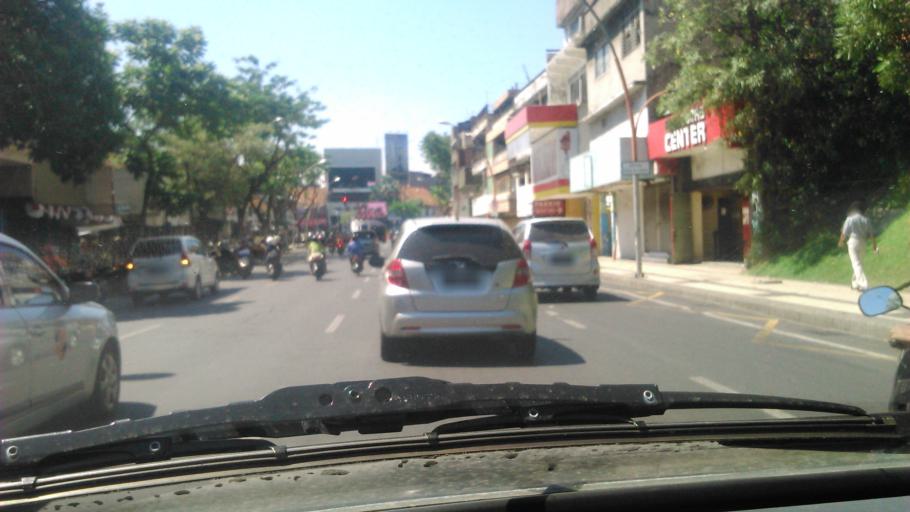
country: ID
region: East Java
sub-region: Kota Surabaya
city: Surabaya
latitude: -7.2575
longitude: 112.7336
